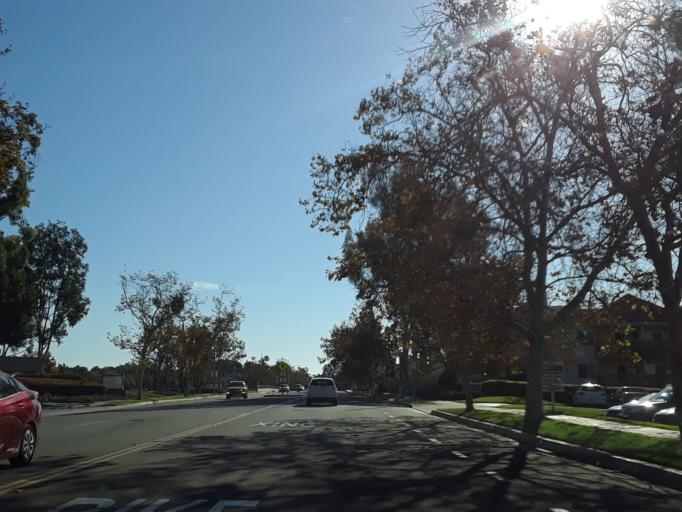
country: US
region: California
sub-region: Orange County
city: Irvine
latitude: 33.6794
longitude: -117.8014
